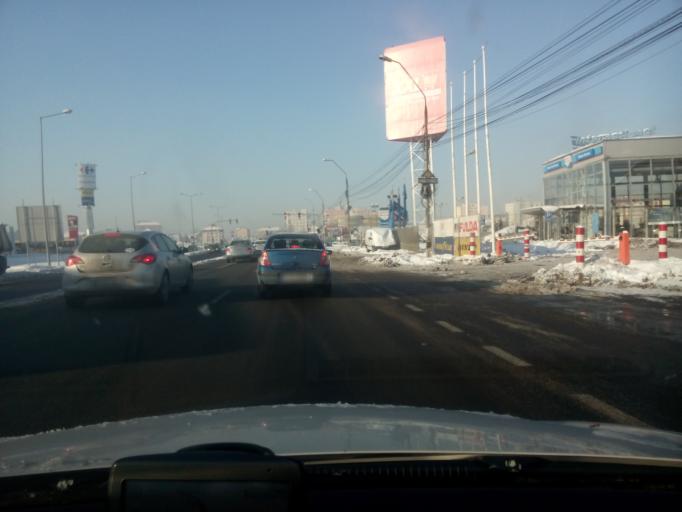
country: RO
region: Sibiu
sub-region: Municipiul Sibiu
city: Sibiu
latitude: 45.7781
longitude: 24.1714
